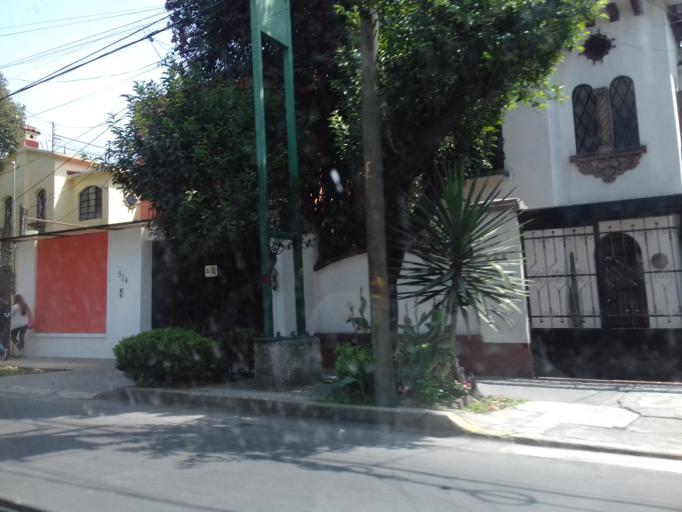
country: MX
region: Mexico City
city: Colonia del Valle
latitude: 19.3834
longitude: -99.1649
